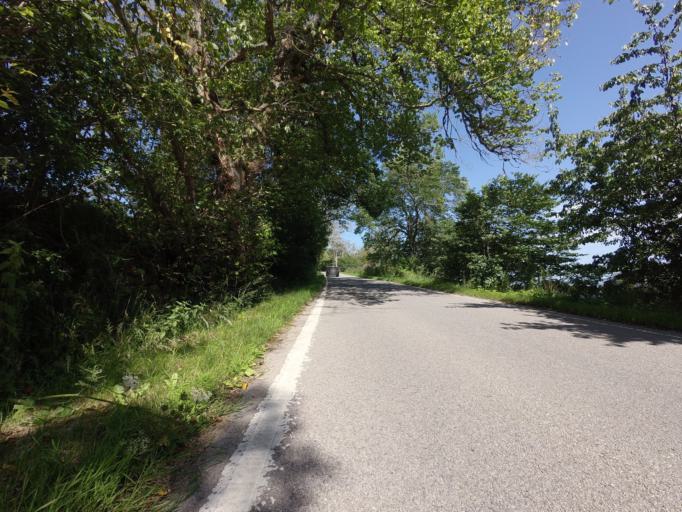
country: GB
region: Scotland
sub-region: Highland
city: Dingwall
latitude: 57.6130
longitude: -4.4139
